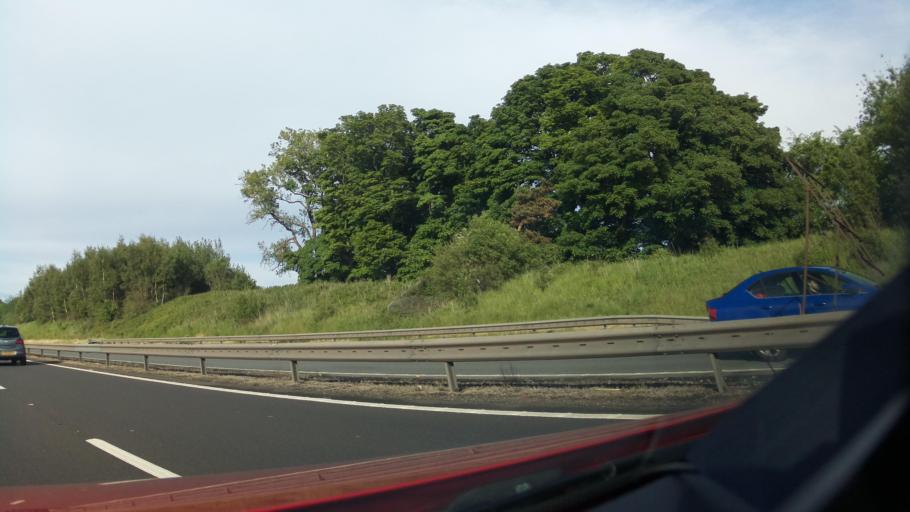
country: GB
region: Scotland
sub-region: Edinburgh
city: Kirkliston
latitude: 55.9683
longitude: -3.3930
